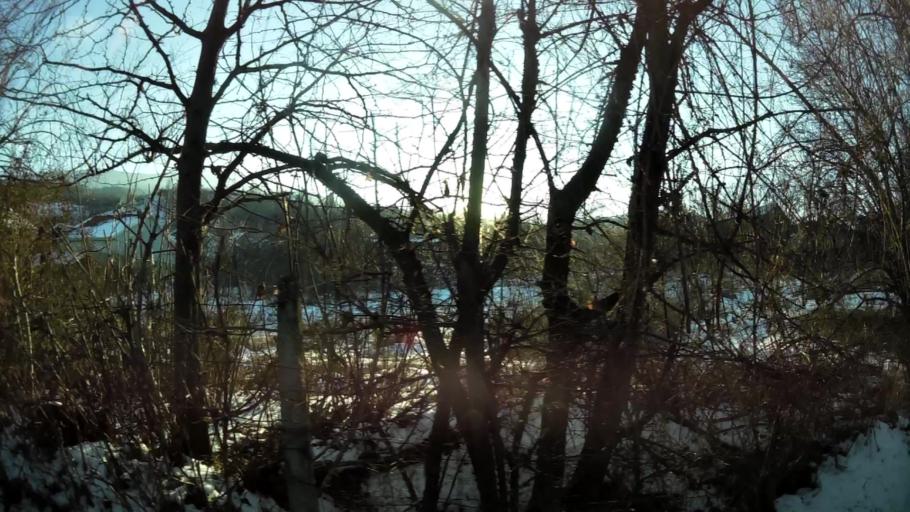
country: MK
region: Karpos
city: Skopje
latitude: 41.9908
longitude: 21.4019
